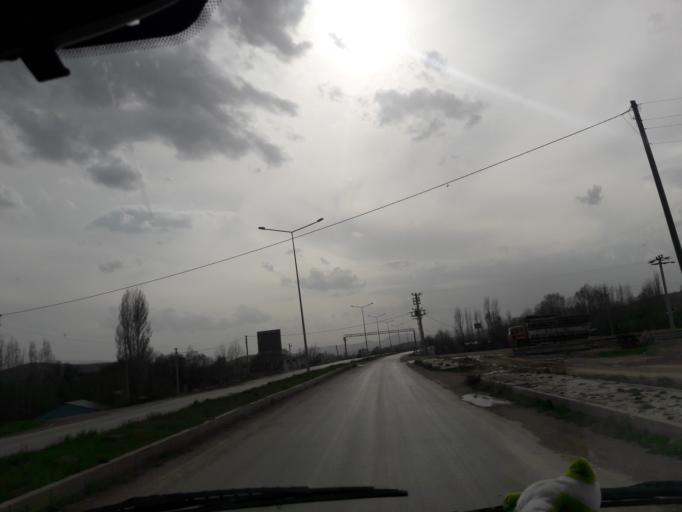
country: TR
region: Gumushane
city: Siran
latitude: 40.1774
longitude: 39.1097
